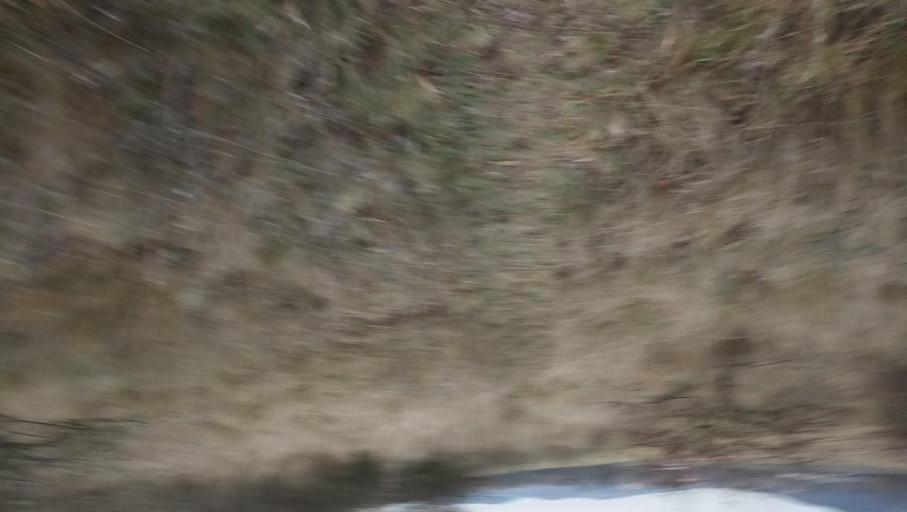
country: HU
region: Pest
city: Pilisborosjeno
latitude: 47.6129
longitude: 18.9802
